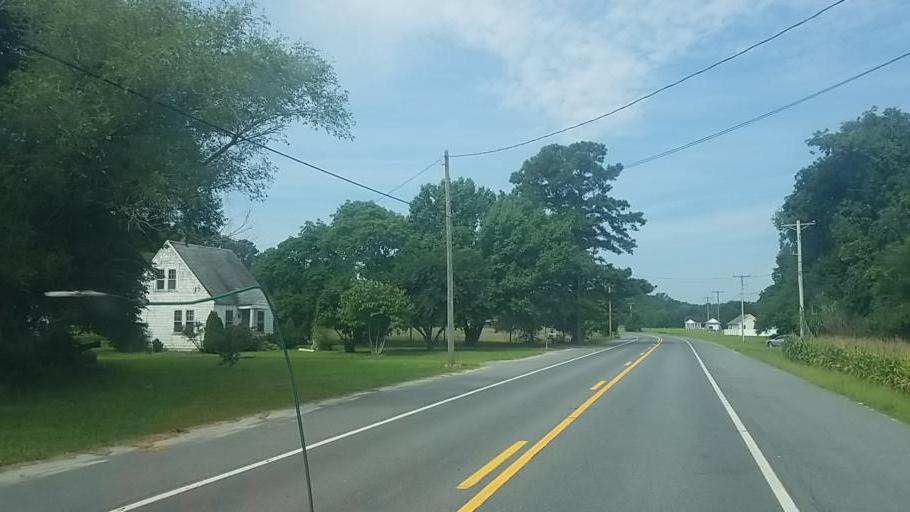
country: US
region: Delaware
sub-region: Sussex County
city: Ocean View
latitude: 38.5479
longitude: -75.1543
